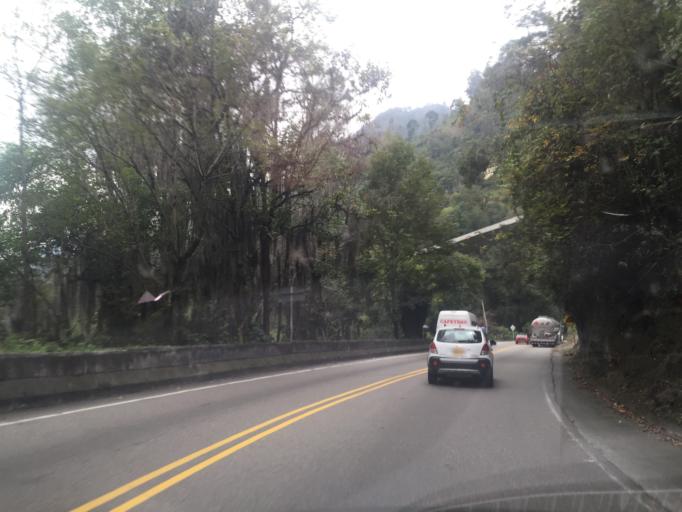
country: CO
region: Tolima
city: Cajamarca
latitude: 4.4340
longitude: -75.4596
